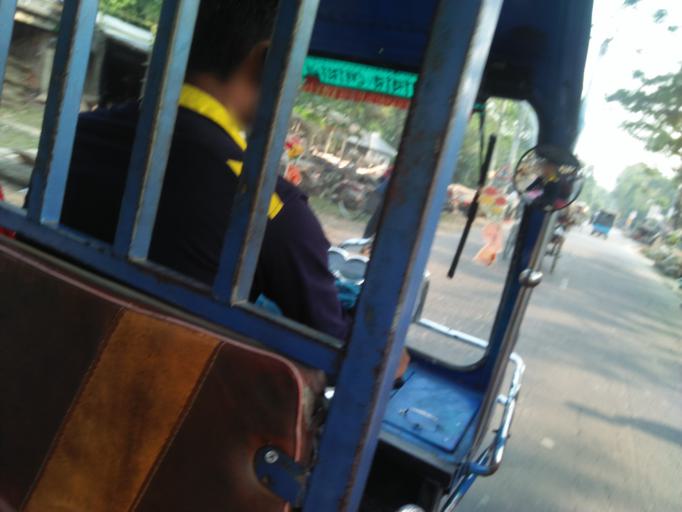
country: BD
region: Barisal
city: Bhola
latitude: 22.7251
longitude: 90.6355
